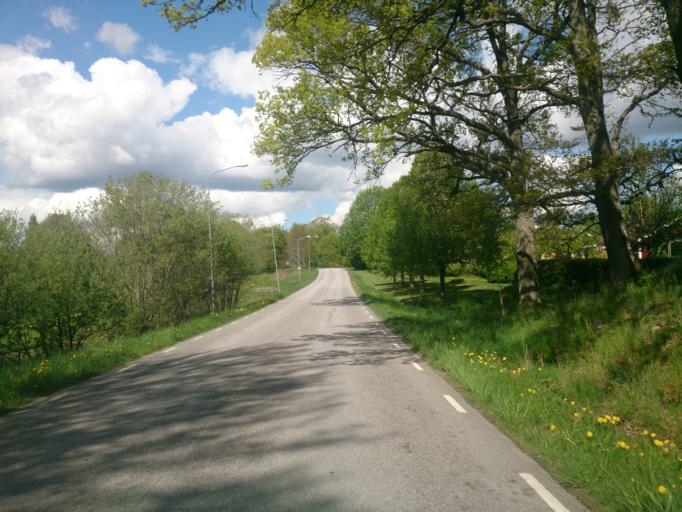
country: SE
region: OEstergoetland
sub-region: Atvidabergs Kommun
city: Atvidaberg
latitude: 58.2012
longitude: 15.9738
